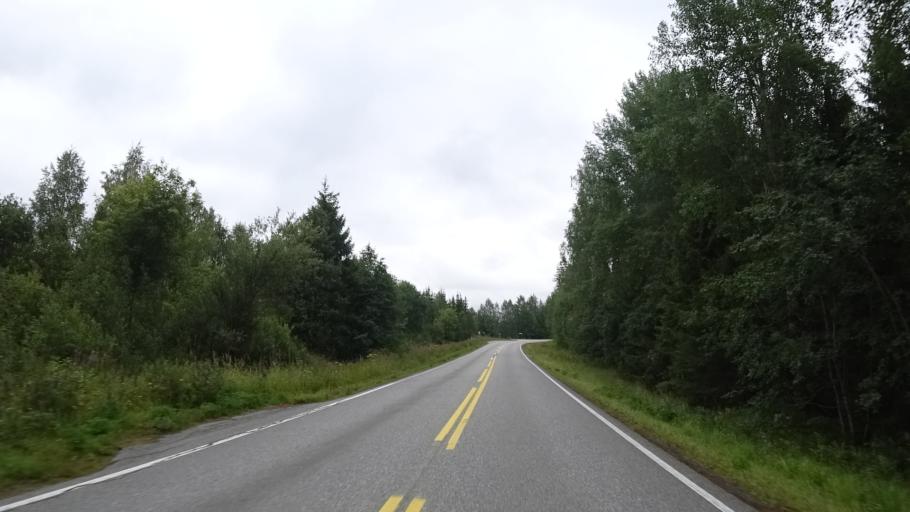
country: FI
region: North Karelia
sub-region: Pielisen Karjala
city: Lieksa
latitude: 63.2804
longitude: 30.6112
